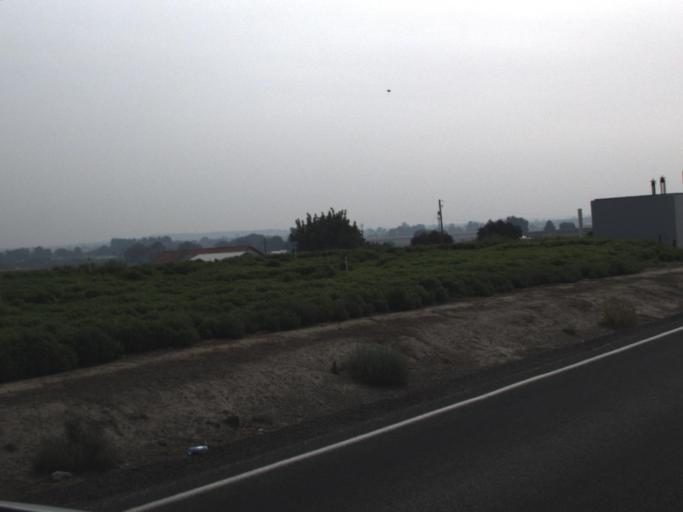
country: US
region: Washington
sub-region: Yakima County
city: Sunnyside
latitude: 46.3409
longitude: -119.9790
